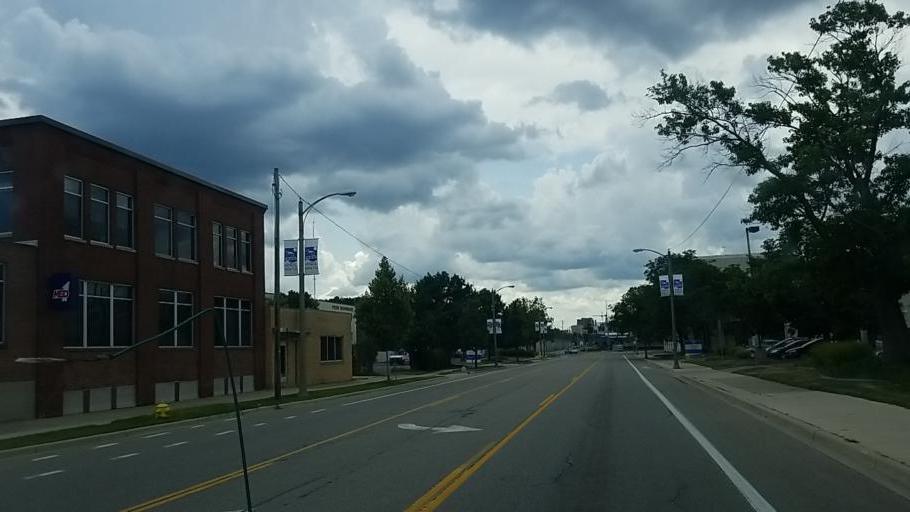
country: US
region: Michigan
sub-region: Kent County
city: Grand Rapids
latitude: 42.9838
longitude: -85.6708
